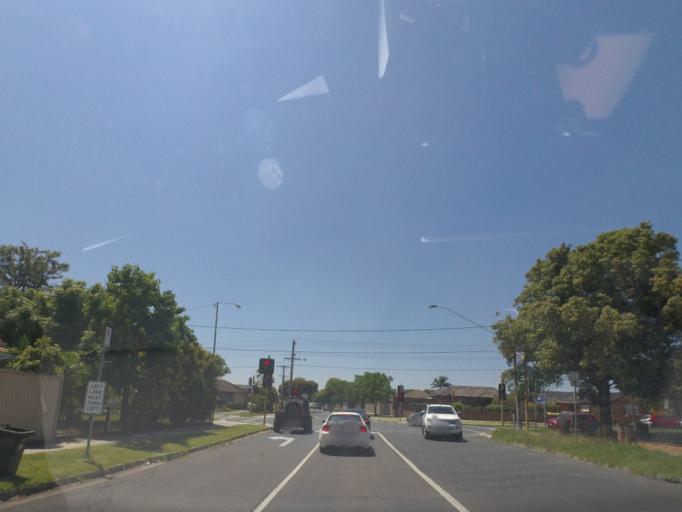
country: AU
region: Victoria
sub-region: Moreland
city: Hadfield
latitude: -37.7172
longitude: 144.9408
